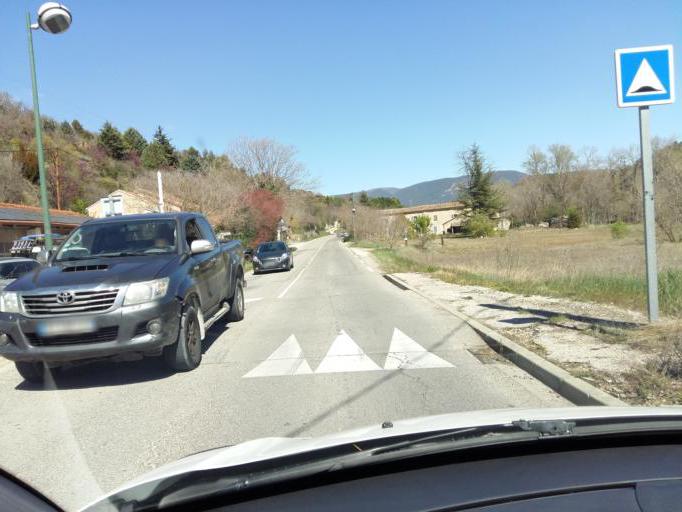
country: FR
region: Provence-Alpes-Cote d'Azur
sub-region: Departement du Vaucluse
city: Saignon
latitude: 43.8817
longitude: 5.4210
